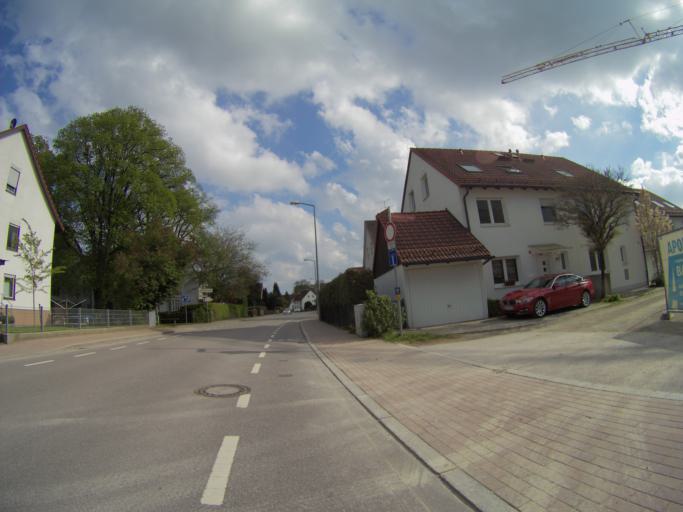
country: DE
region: Bavaria
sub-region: Upper Bavaria
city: Freising
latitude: 48.3940
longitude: 11.7529
